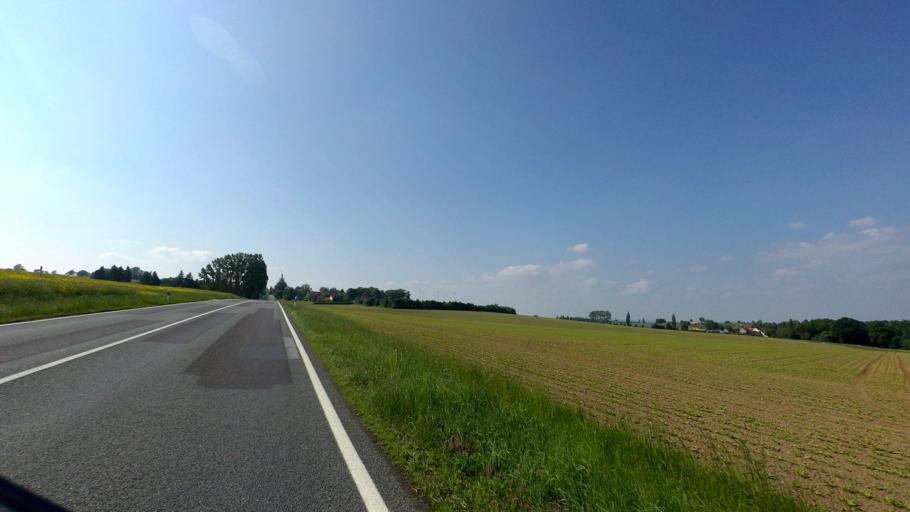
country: DE
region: Saxony
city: Hochkirch
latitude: 51.1440
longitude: 14.5821
